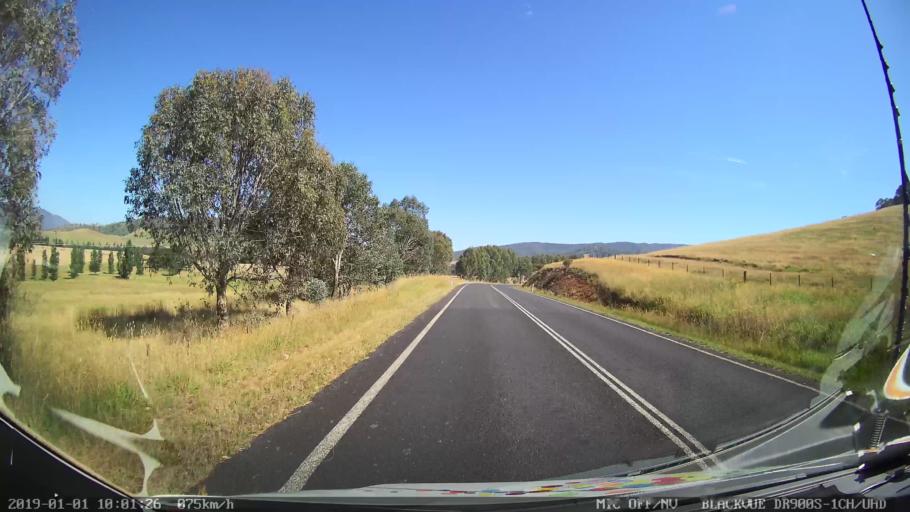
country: AU
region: New South Wales
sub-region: Snowy River
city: Jindabyne
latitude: -36.1918
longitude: 148.1010
